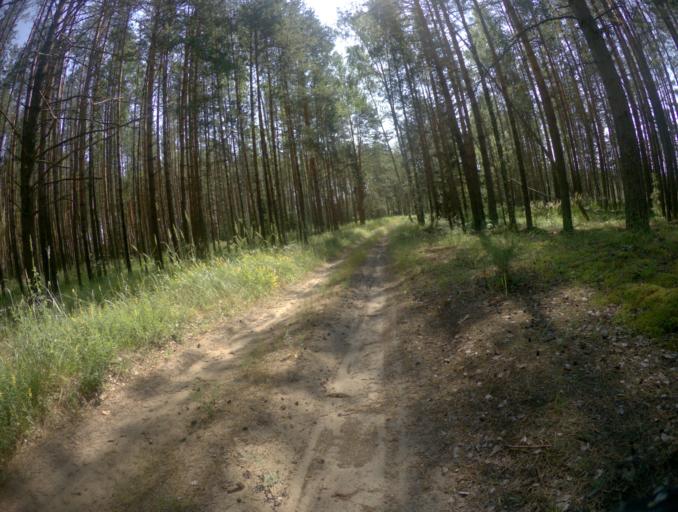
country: RU
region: Vladimir
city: Vyazniki
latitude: 56.3518
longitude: 42.2195
